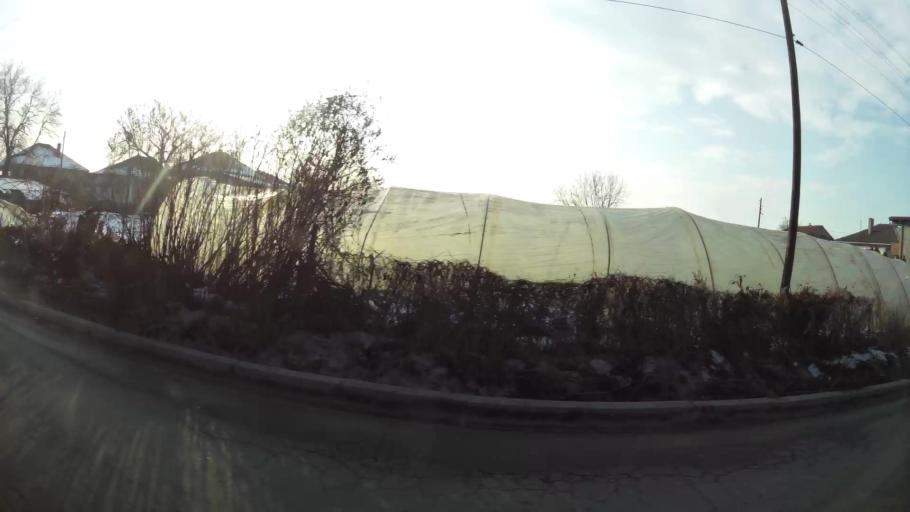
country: MK
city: Creshevo
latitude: 42.0284
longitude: 21.5129
